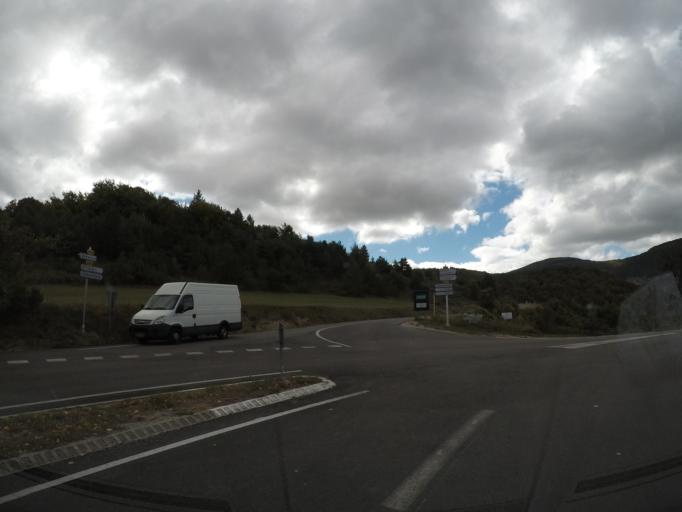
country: FR
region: Provence-Alpes-Cote d'Azur
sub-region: Departement du Vaucluse
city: Sault
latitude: 44.1821
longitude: 5.5100
